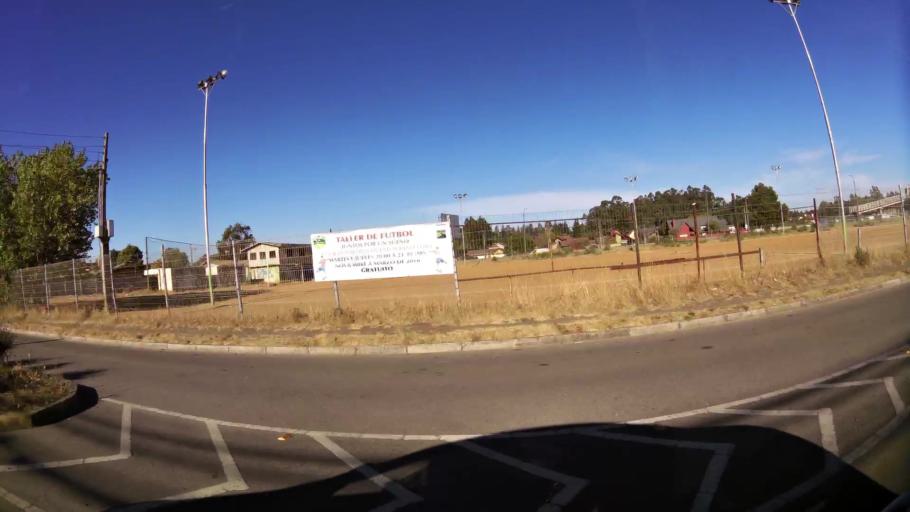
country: CL
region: Biobio
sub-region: Provincia de Concepcion
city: Concepcion
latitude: -36.8336
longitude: -73.1021
